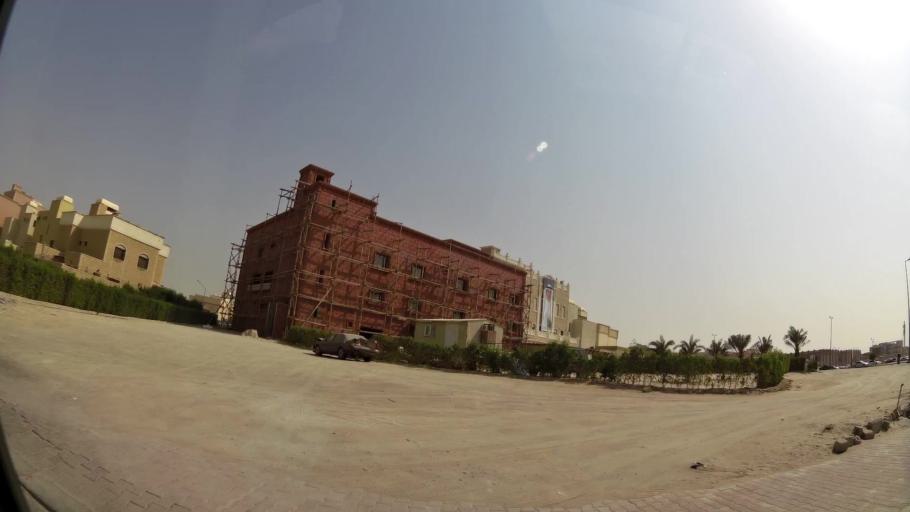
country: KW
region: Muhafazat al Jahra'
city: Al Jahra'
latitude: 29.3156
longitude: 47.7100
